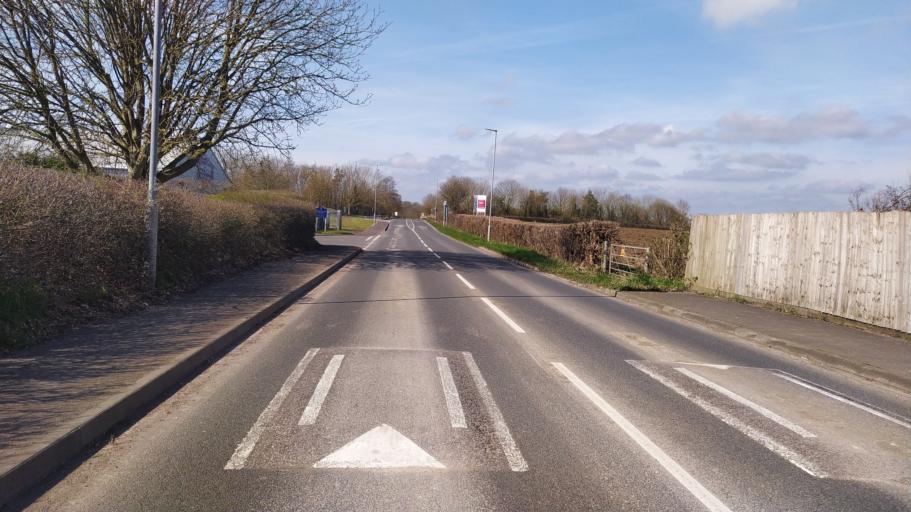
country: GB
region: England
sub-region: Somerset
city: Ilchester
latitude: 51.0124
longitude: -2.6823
